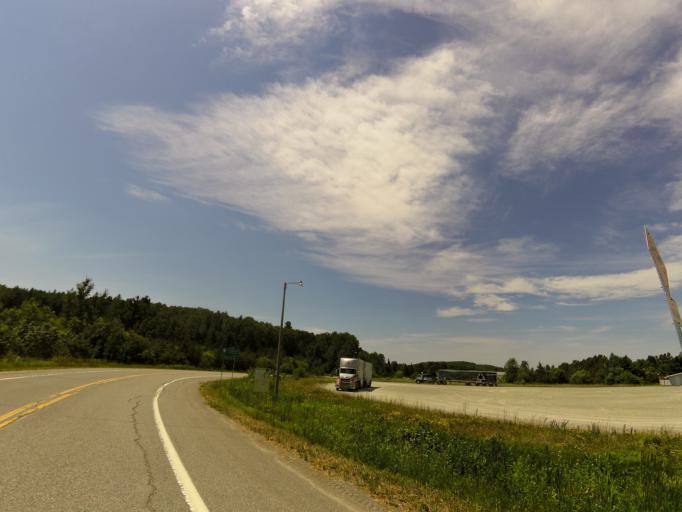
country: CA
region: Quebec
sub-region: Abitibi-Temiscamingue
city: Ville-Marie
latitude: 47.2950
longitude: -79.4241
